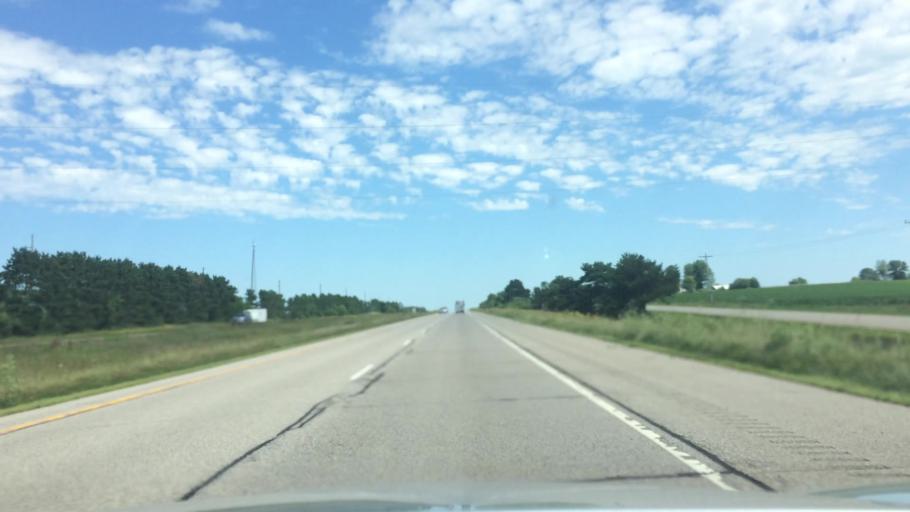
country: US
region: Wisconsin
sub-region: Marquette County
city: Westfield
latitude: 43.8310
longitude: -89.4823
